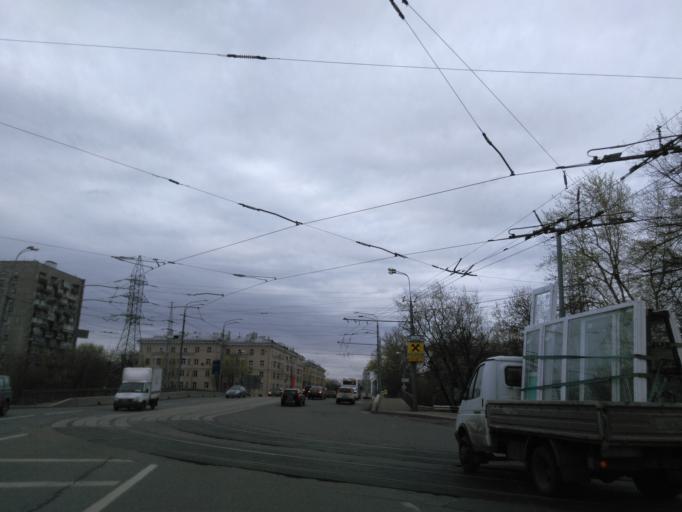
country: RU
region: Moscow
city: Pokrovskoye-Streshnevo
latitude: 55.8360
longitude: 37.4540
